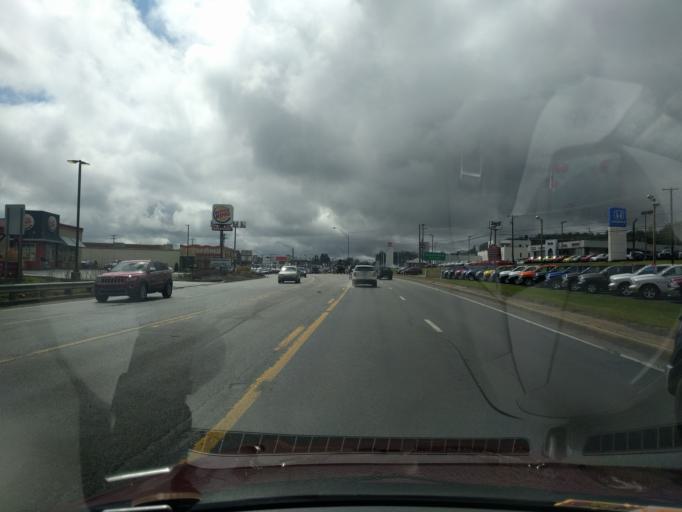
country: US
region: West Virginia
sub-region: Raleigh County
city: Beckley
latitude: 37.8077
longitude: -81.1852
